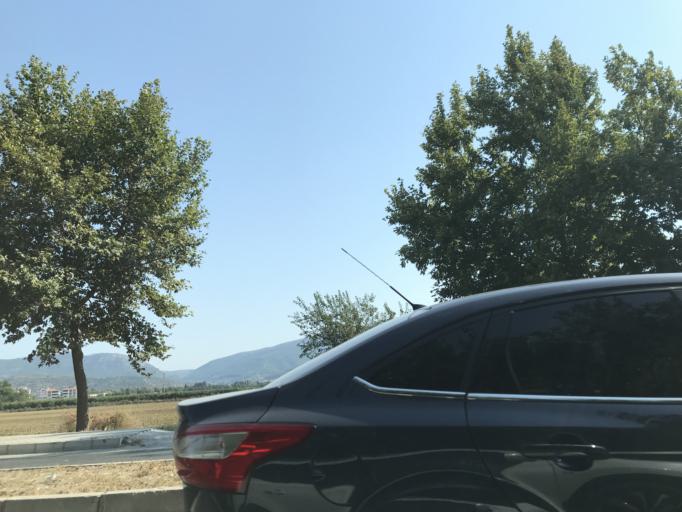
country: TR
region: Izmir
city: Selcuk
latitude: 37.9485
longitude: 27.3620
